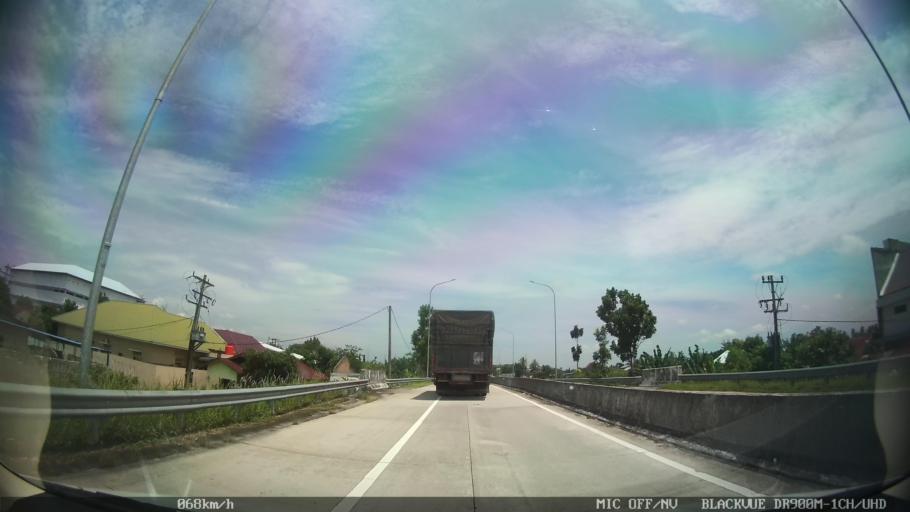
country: ID
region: North Sumatra
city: Perbaungan
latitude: 3.5532
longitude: 98.8872
